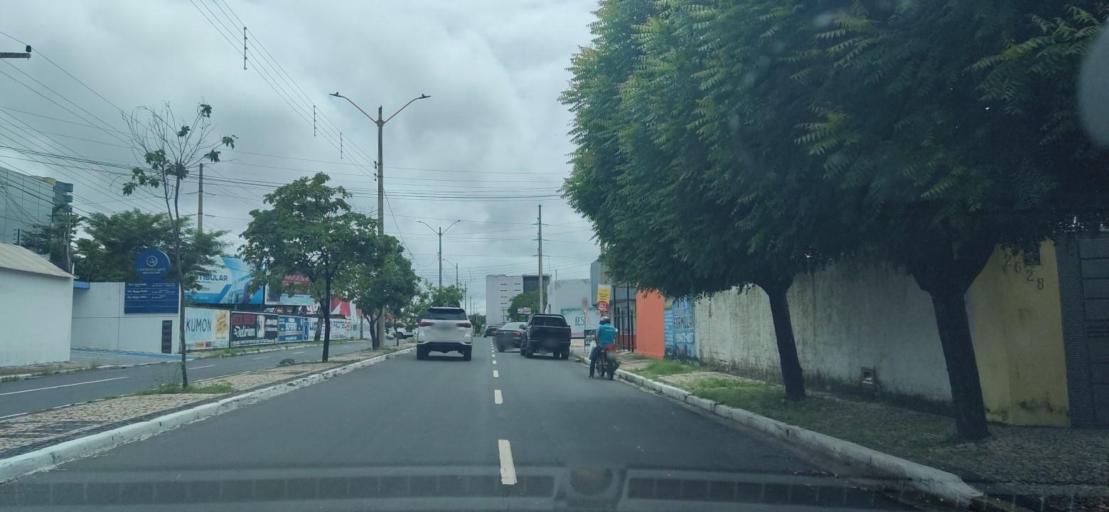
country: BR
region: Piaui
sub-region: Teresina
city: Teresina
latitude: -5.0726
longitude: -42.7758
